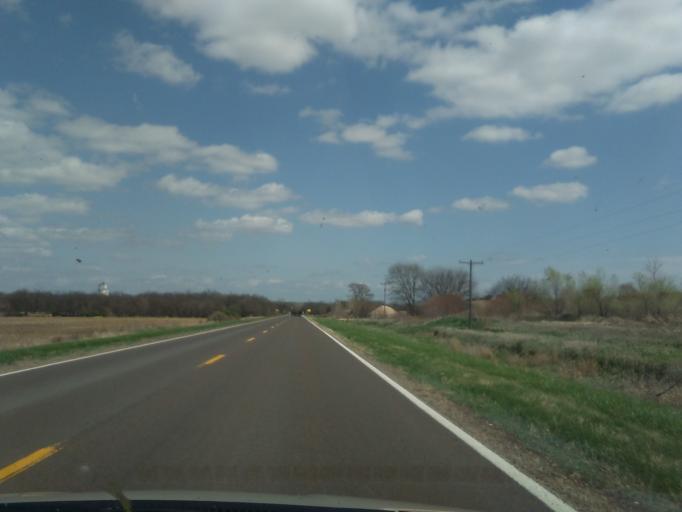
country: US
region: Nebraska
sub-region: Thayer County
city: Hebron
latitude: 40.2489
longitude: -97.5713
